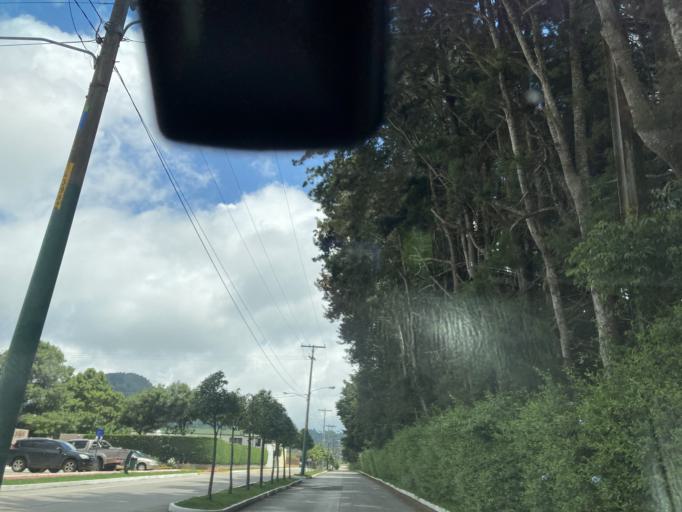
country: GT
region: Guatemala
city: San Jose Pinula
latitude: 14.5410
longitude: -90.4296
